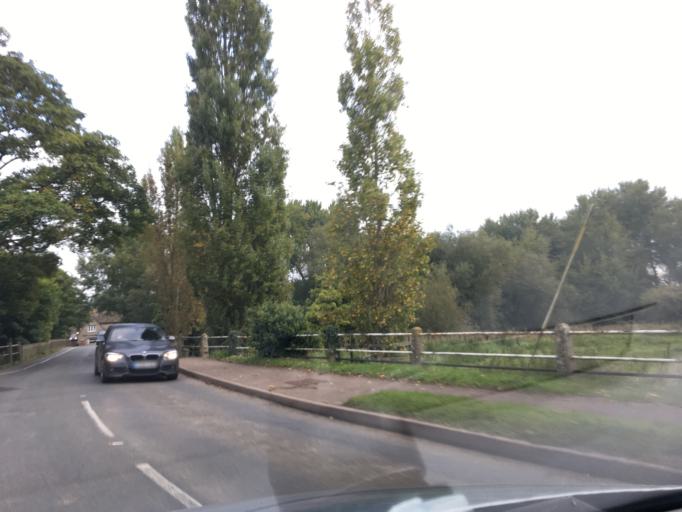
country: GB
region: England
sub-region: Oxfordshire
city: Kidlington
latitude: 51.8208
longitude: -1.2353
